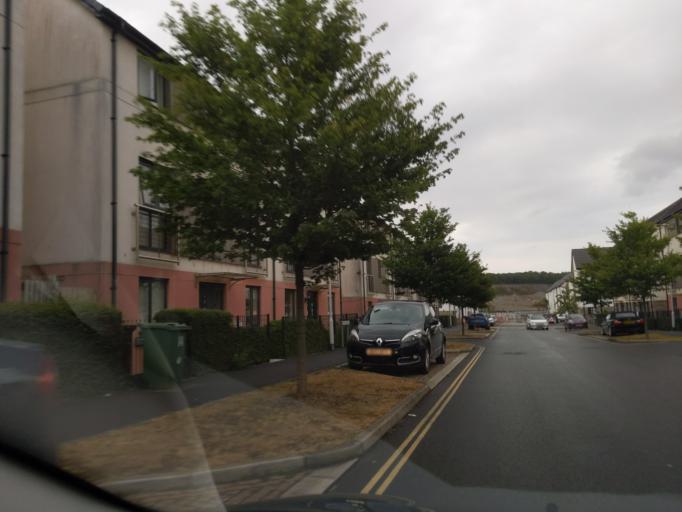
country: GB
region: England
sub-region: Plymouth
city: Plymstock
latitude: 50.3686
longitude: -4.0983
